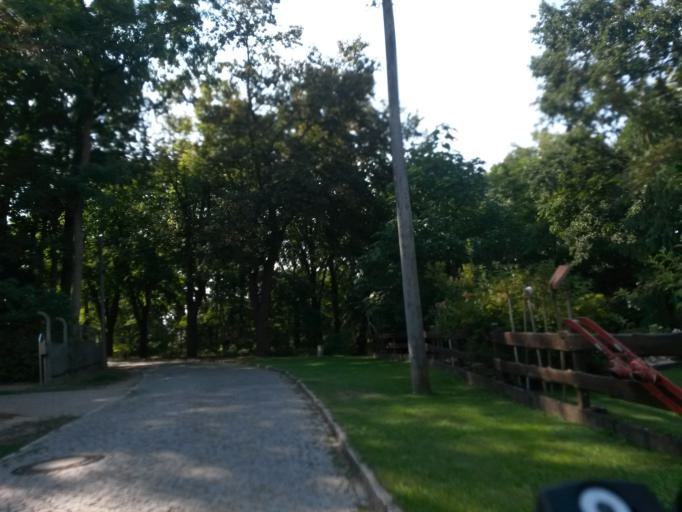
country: DE
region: Saxony-Anhalt
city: Nudersdorf
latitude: 51.9168
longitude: 12.5923
